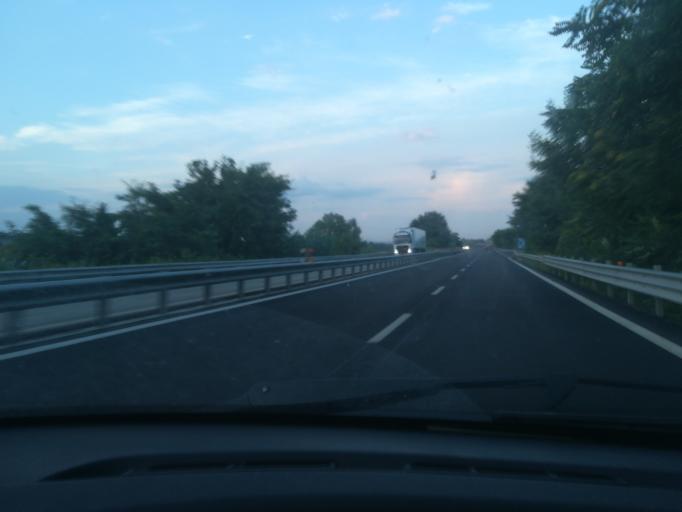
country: IT
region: The Marches
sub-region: Provincia di Macerata
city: Zona Industriale
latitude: 43.2566
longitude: 13.4559
